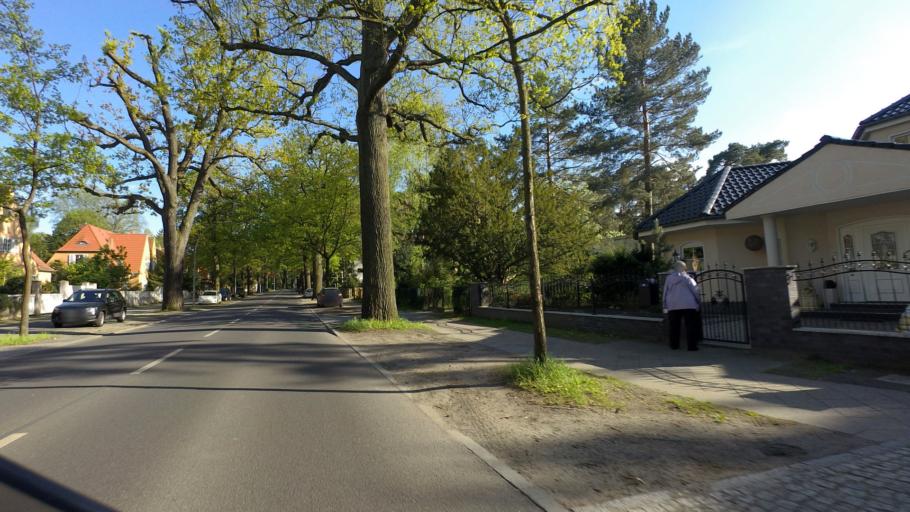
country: DE
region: Berlin
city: Frohnau
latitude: 52.6426
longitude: 13.3020
